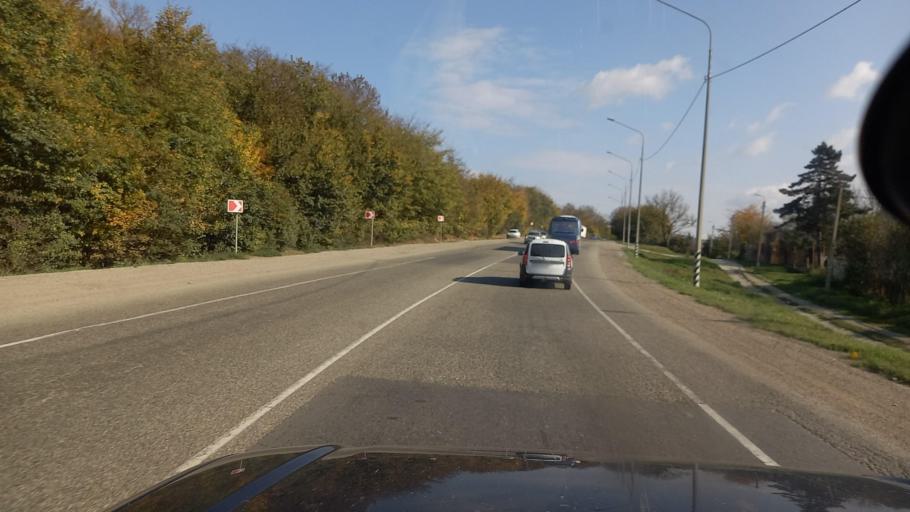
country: RU
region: Krasnodarskiy
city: Verkhnebakanskiy
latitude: 44.8622
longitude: 37.7375
